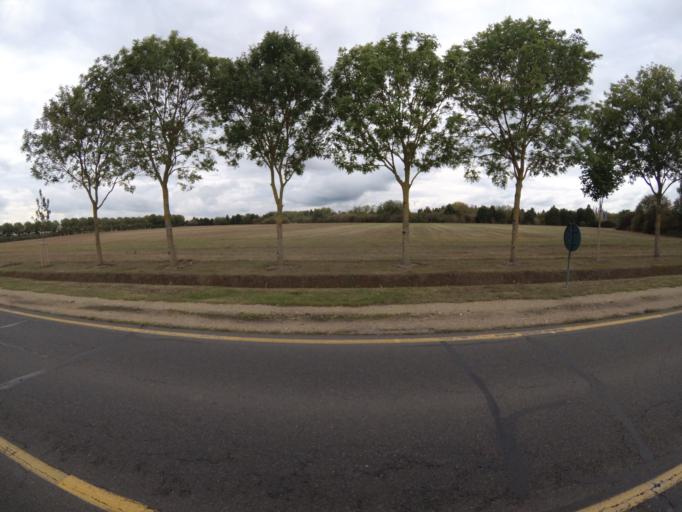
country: FR
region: Ile-de-France
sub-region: Departement de Seine-et-Marne
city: Coupvray
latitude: 48.8765
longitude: 2.7994
